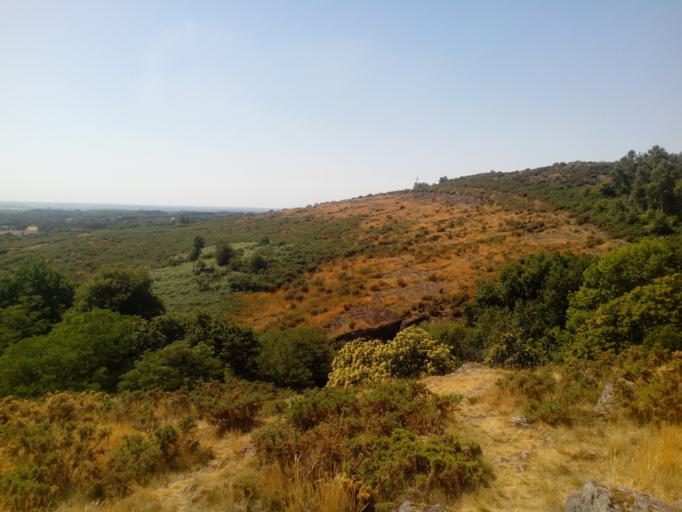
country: FR
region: Brittany
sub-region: Departement du Morbihan
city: Campeneac
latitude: 47.9841
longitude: -2.2656
